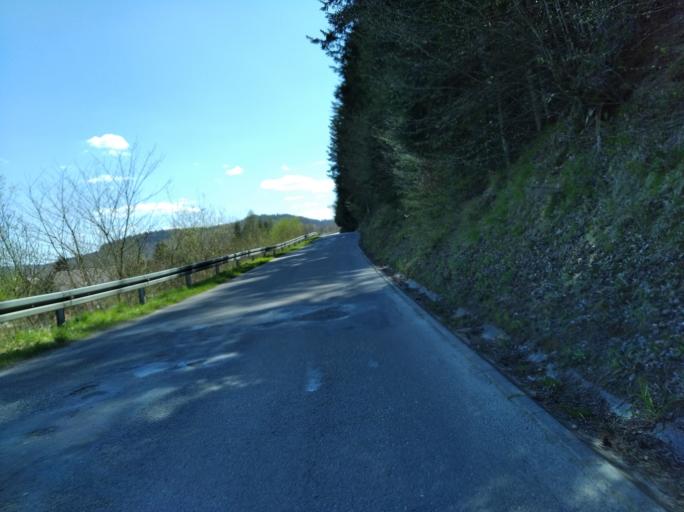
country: PL
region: Subcarpathian Voivodeship
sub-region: Powiat brzozowski
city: Dydnia
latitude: 49.6940
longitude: 22.2024
